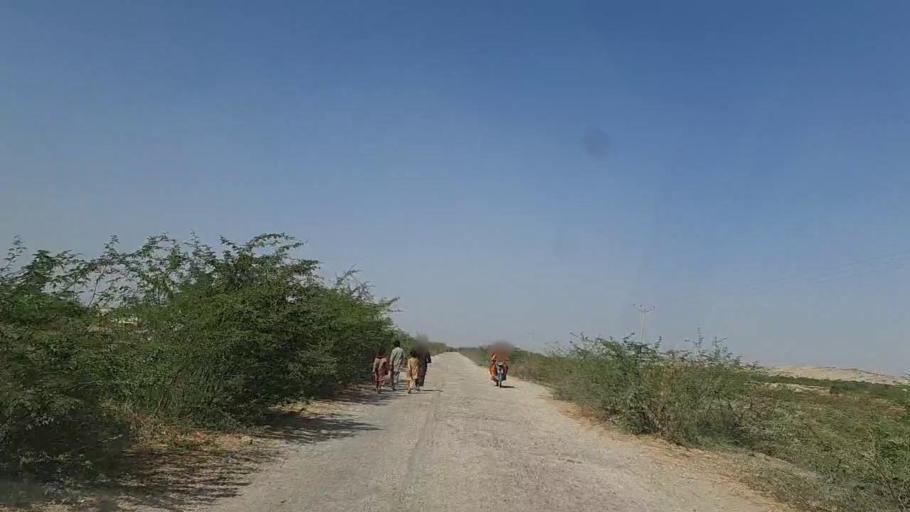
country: PK
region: Sindh
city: Naukot
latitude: 24.6261
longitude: 69.2888
